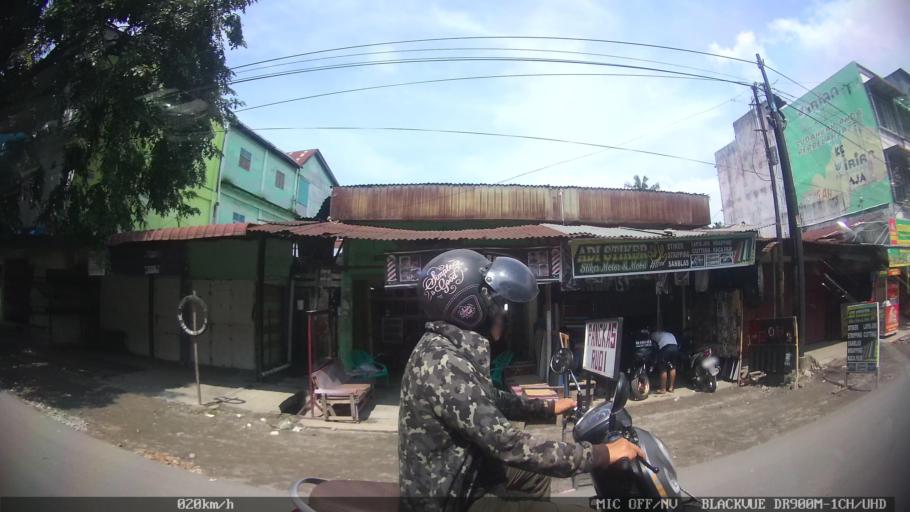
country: ID
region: North Sumatra
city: Medan
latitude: 3.6289
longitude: 98.6623
